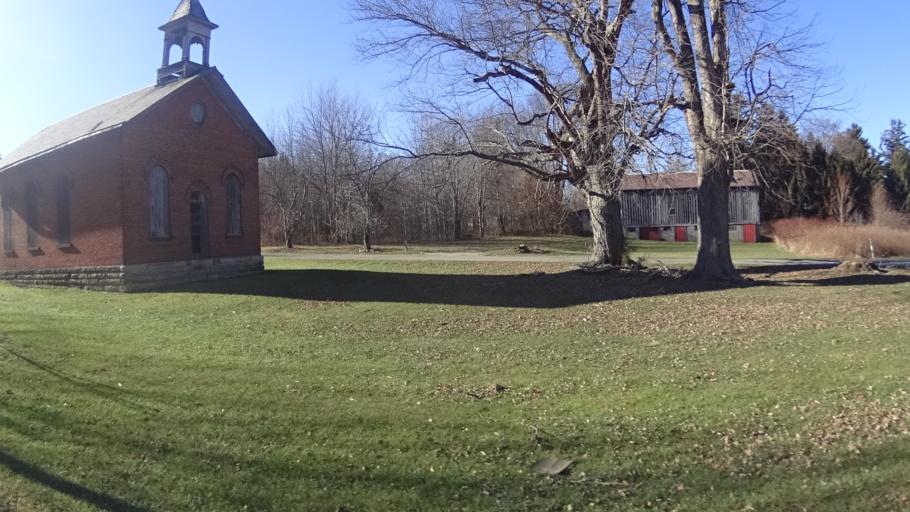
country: US
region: Ohio
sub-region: Lorain County
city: Vermilion-on-the-Lake
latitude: 41.3766
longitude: -82.3223
